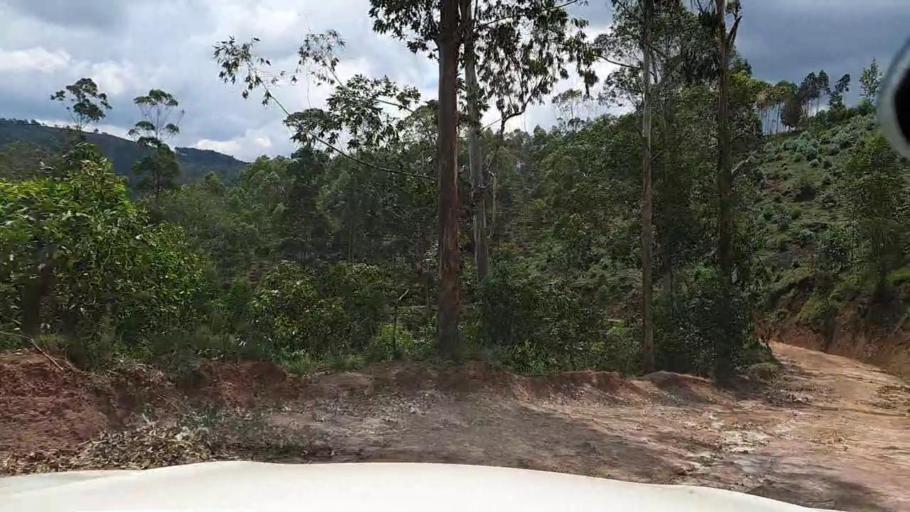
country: RW
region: Southern Province
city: Nzega
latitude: -2.6427
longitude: 29.4780
